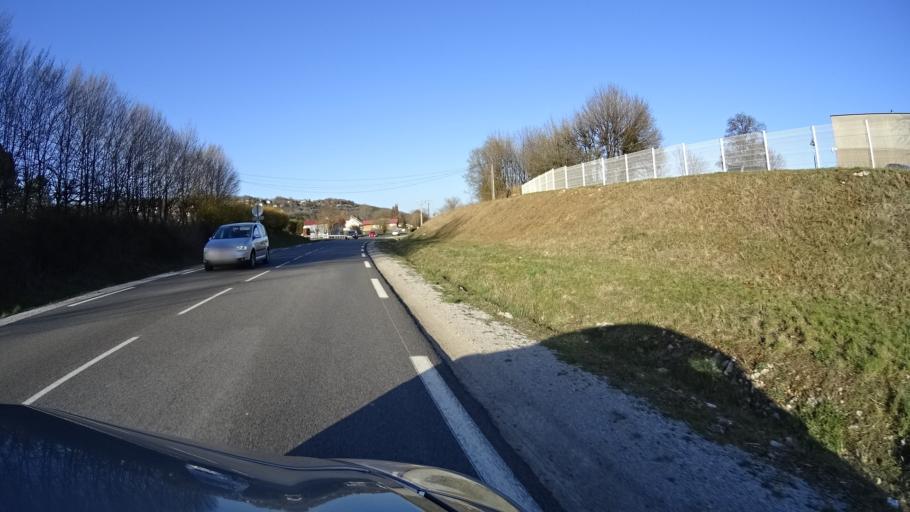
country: FR
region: Franche-Comte
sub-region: Departement du Doubs
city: Beure
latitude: 47.1949
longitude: 6.0214
